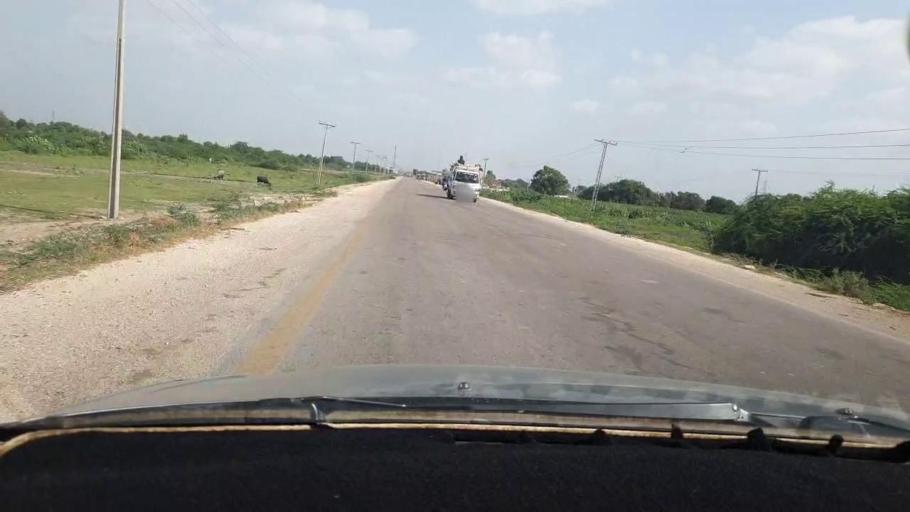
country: PK
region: Sindh
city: Naukot
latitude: 24.8627
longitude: 69.3890
